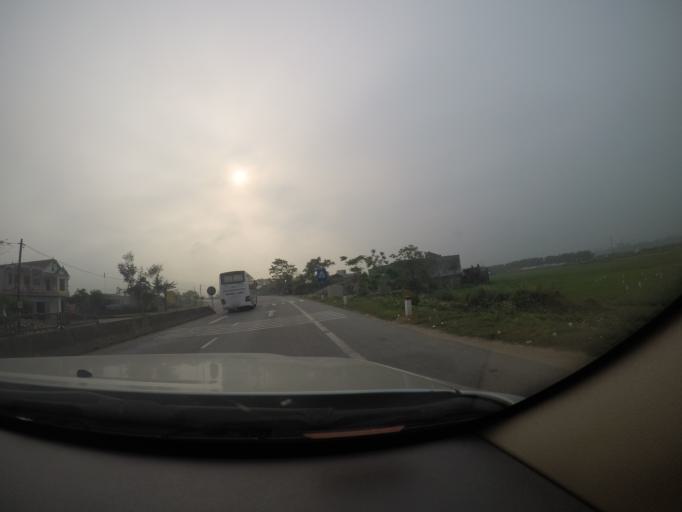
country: VN
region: Ha Tinh
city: Cam Xuyen
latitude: 18.2114
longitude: 106.1109
